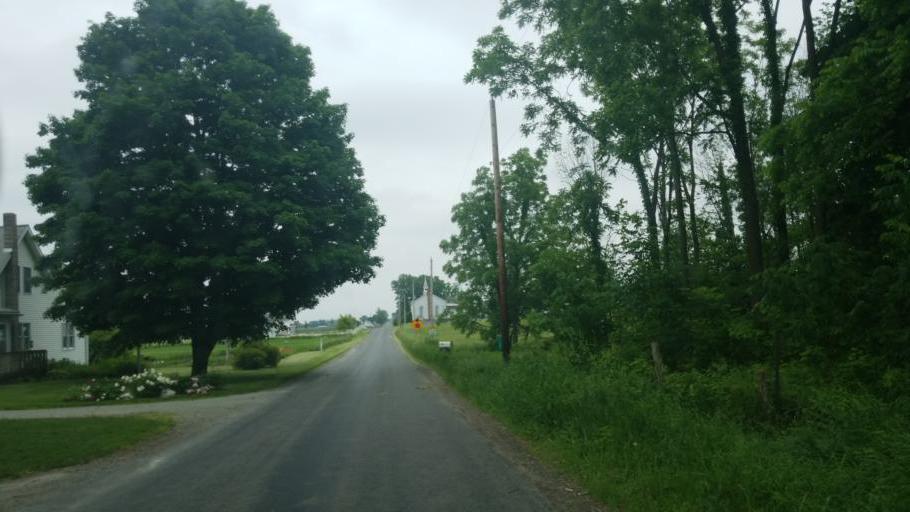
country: US
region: Indiana
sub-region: Elkhart County
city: Wakarusa
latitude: 41.4936
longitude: -86.0825
